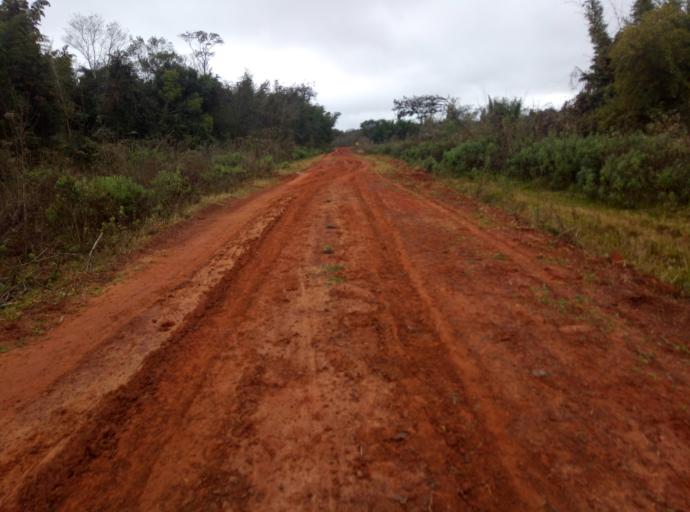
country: PY
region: Caaguazu
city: Doctor Cecilio Baez
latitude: -25.1209
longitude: -56.2133
